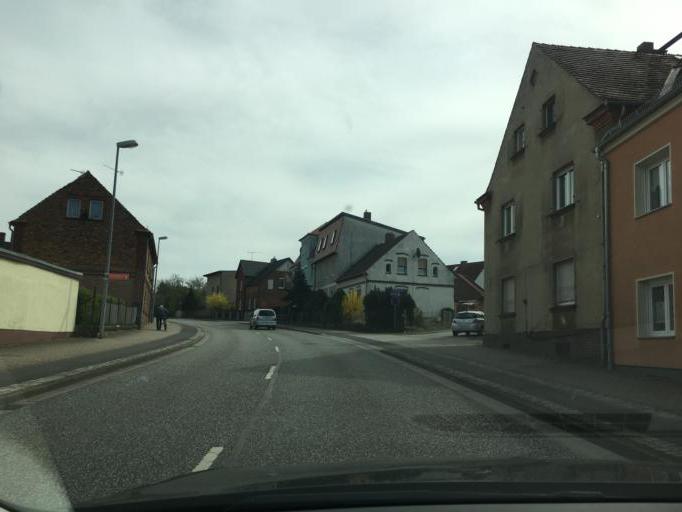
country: DE
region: Brandenburg
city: Spremberg
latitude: 51.5668
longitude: 14.3896
